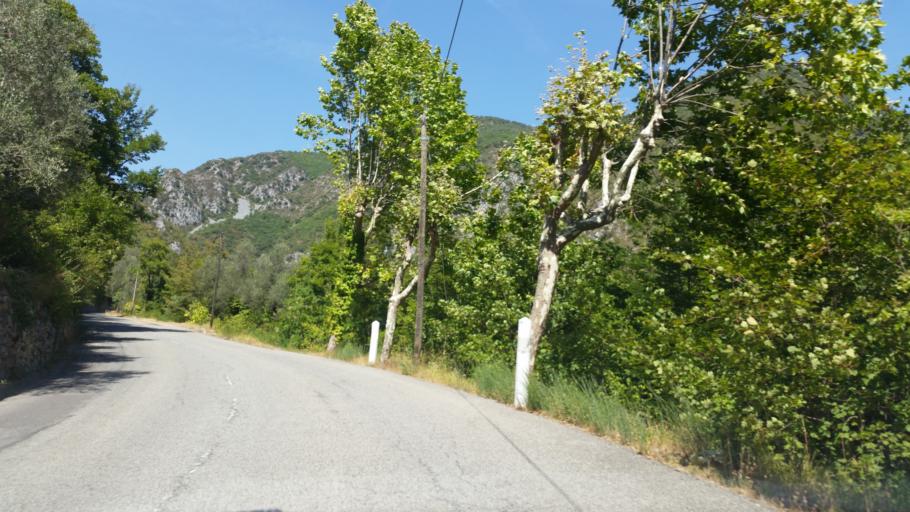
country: FR
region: Provence-Alpes-Cote d'Azur
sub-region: Departement des Alpes-Maritimes
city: Breil-sur-Roya
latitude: 43.9528
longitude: 7.5170
